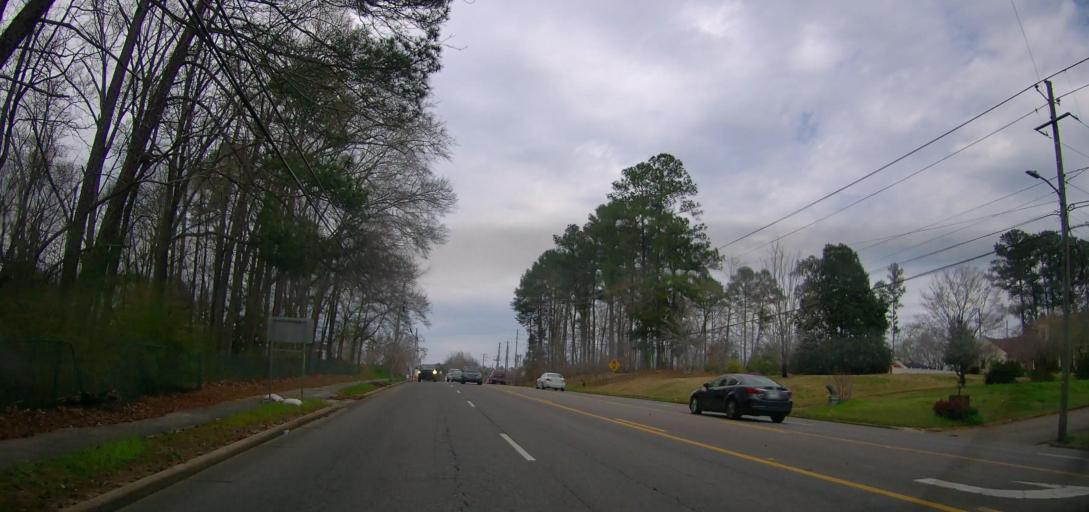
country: US
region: Alabama
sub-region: Marion County
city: Hamilton
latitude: 34.1305
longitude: -87.9901
